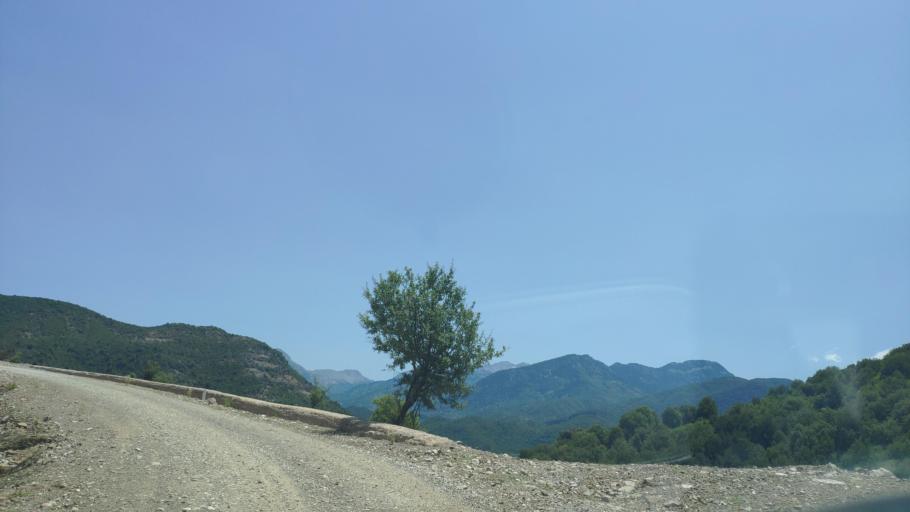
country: GR
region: Thessaly
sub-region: Nomos Kardhitsas
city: Anthiro
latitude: 39.1683
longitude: 21.3713
